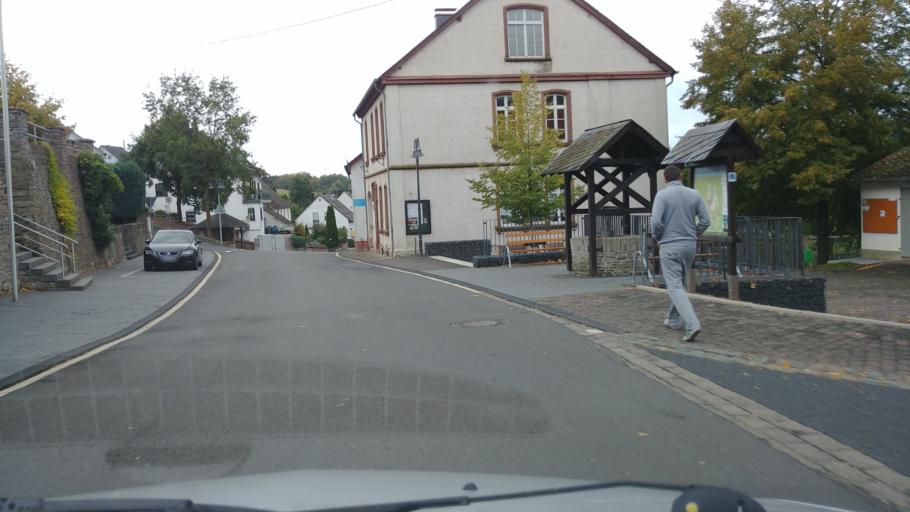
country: DE
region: Rheinland-Pfalz
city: Horath
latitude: 49.8114
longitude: 6.9862
